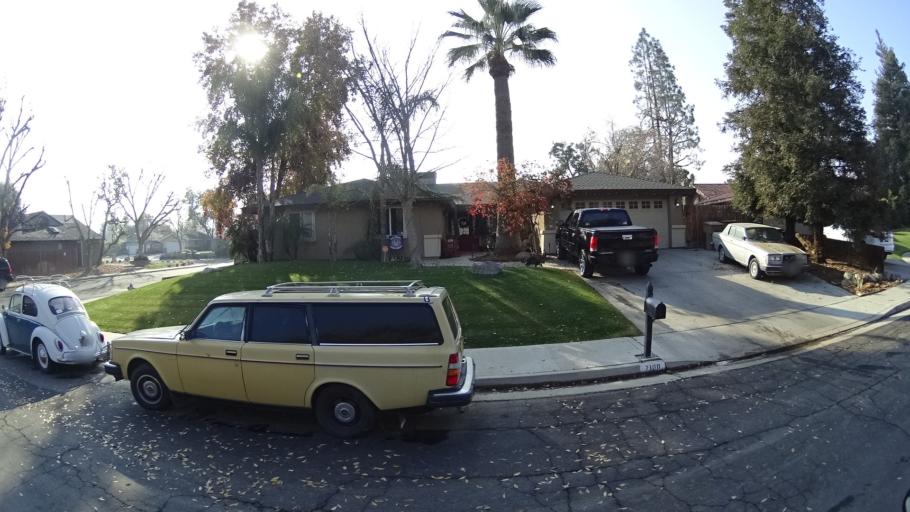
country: US
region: California
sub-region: Kern County
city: Greenacres
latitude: 35.3386
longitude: -119.0813
